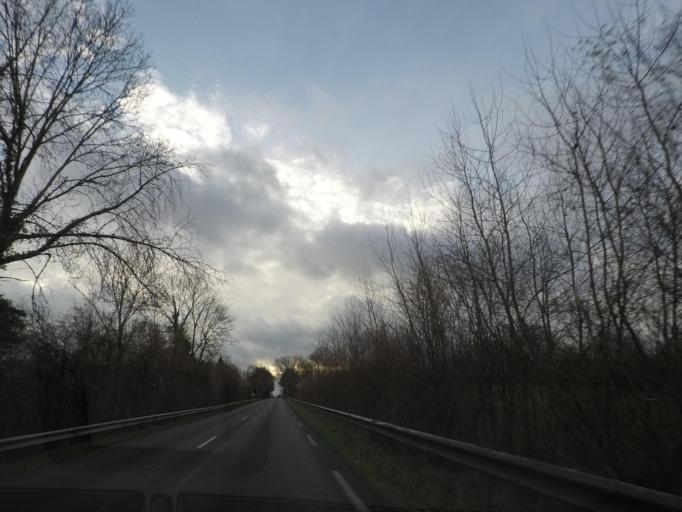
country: FR
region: Pays de la Loire
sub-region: Departement de la Sarthe
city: Cherre
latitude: 48.1335
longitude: 0.6973
